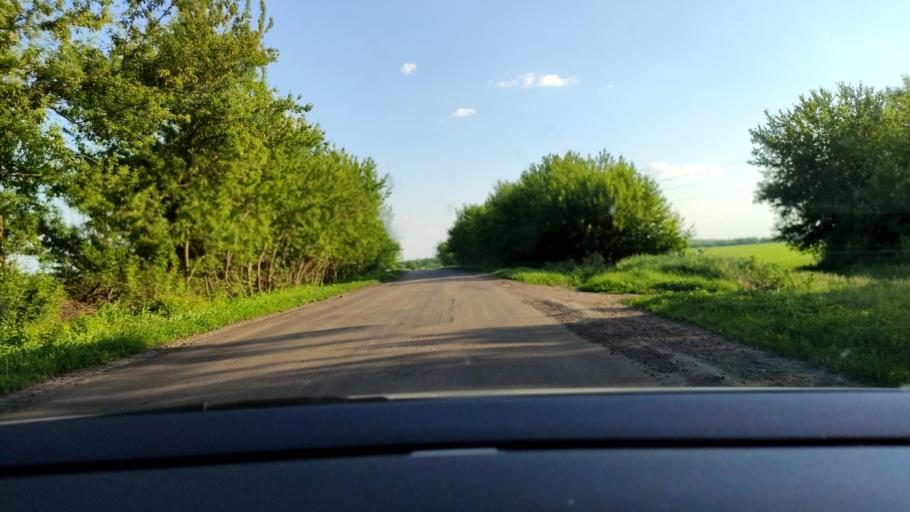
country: RU
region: Voronezj
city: Kashirskoye
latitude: 51.5219
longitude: 39.8350
